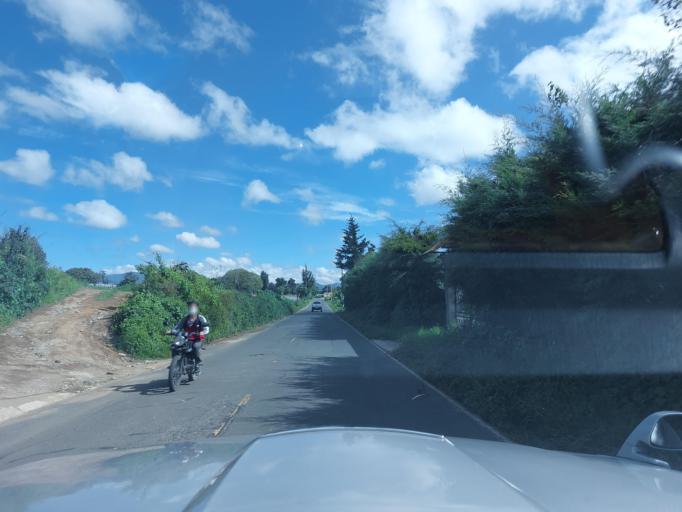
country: GT
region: Chimaltenango
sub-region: Municipio de Zaragoza
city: Zaragoza
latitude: 14.6625
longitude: -90.8987
